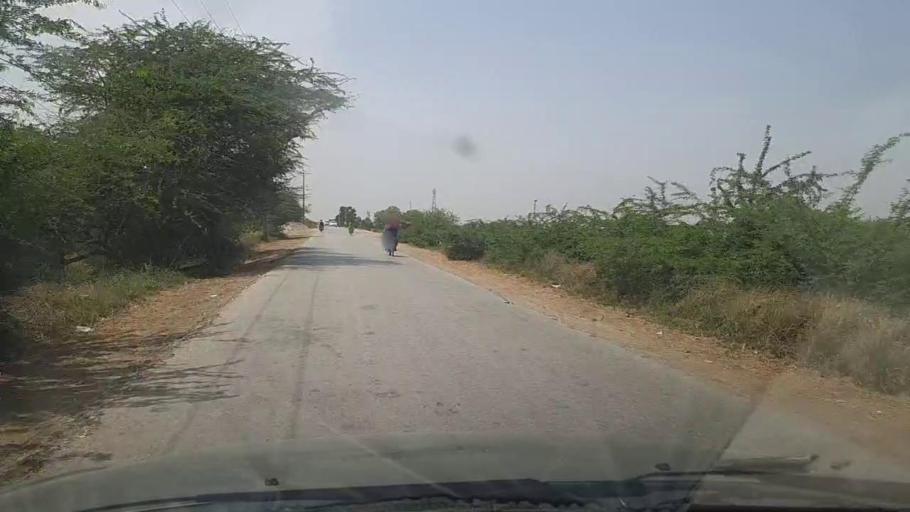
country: PK
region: Sindh
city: Bhiria
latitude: 26.9047
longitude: 68.2027
